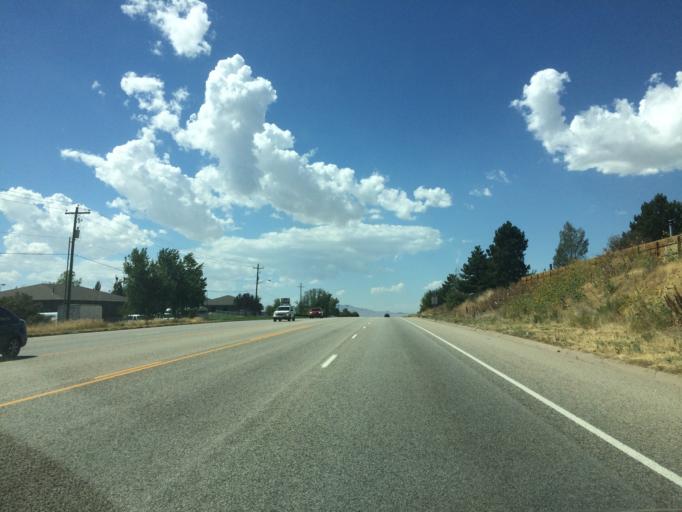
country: US
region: Utah
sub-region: Davis County
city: South Weber
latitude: 41.1065
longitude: -111.9202
